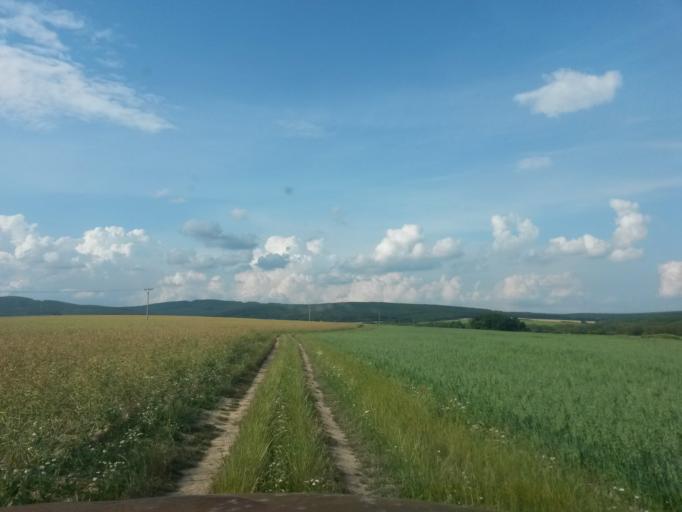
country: SK
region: Kosicky
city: Moldava nad Bodvou
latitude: 48.6551
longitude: 21.1073
